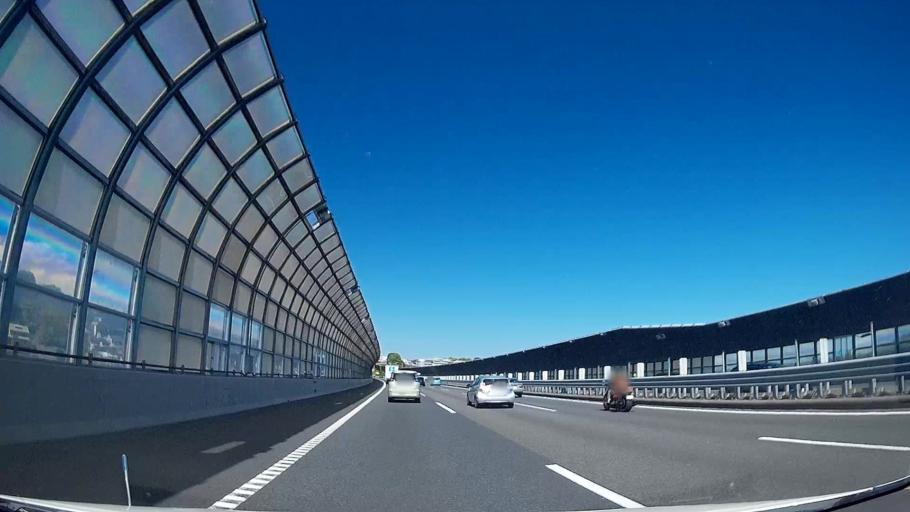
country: JP
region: Kanagawa
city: Hadano
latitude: 35.3599
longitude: 139.2494
